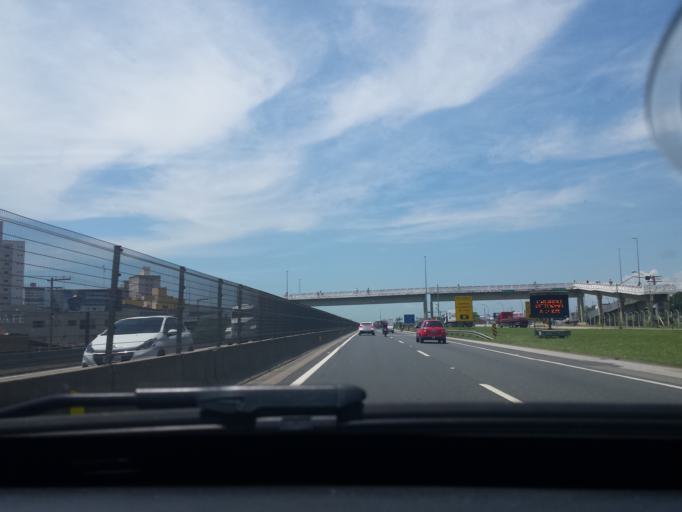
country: BR
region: Santa Catarina
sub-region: Itapema
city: Itapema
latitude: -27.1248
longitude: -48.6095
